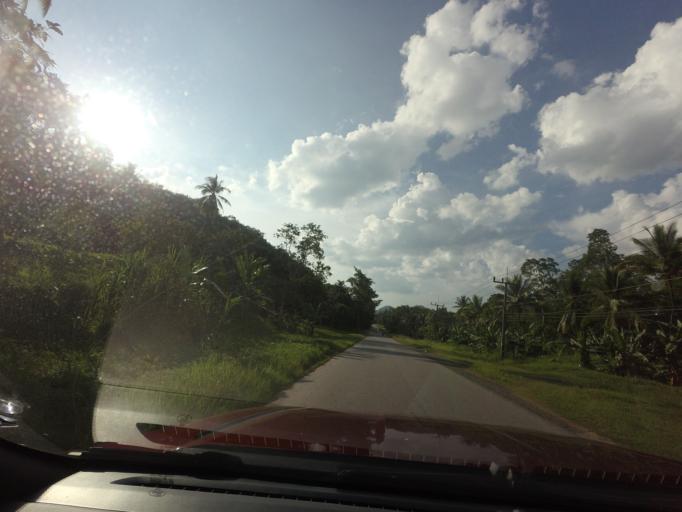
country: TH
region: Yala
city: Ban Nang Sata
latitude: 6.2074
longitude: 101.2350
